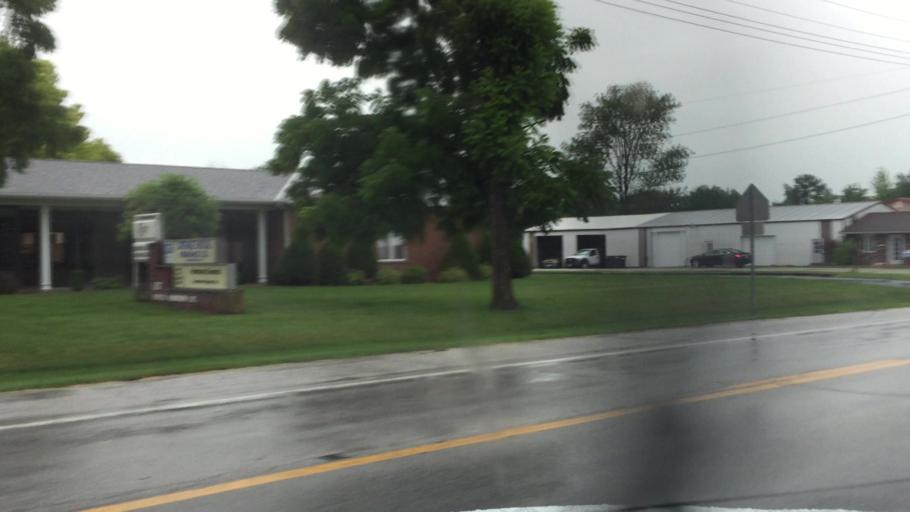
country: US
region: Illinois
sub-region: Hancock County
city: Carthage
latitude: 40.4217
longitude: -91.1362
